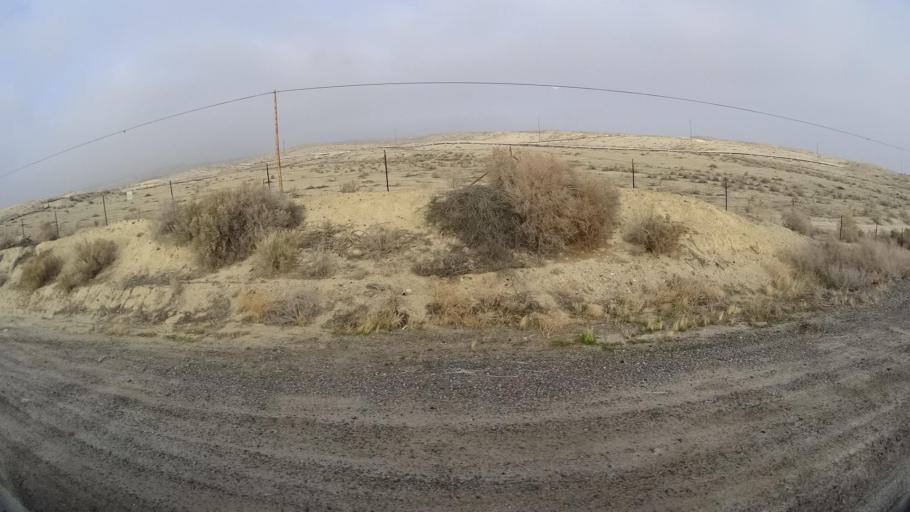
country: US
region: California
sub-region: Kern County
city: Ford City
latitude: 35.2413
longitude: -119.4528
